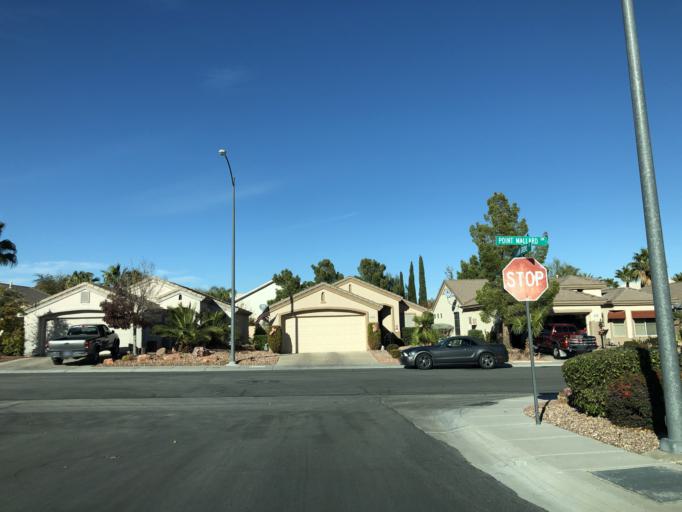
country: US
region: Nevada
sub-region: Clark County
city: Whitney
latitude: 36.0123
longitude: -115.0794
